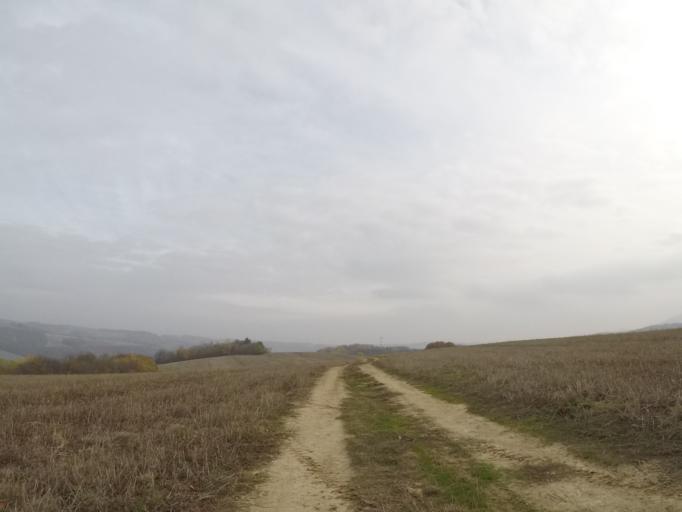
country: SK
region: Presovsky
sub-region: Okres Presov
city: Presov
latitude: 48.9392
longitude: 21.1588
